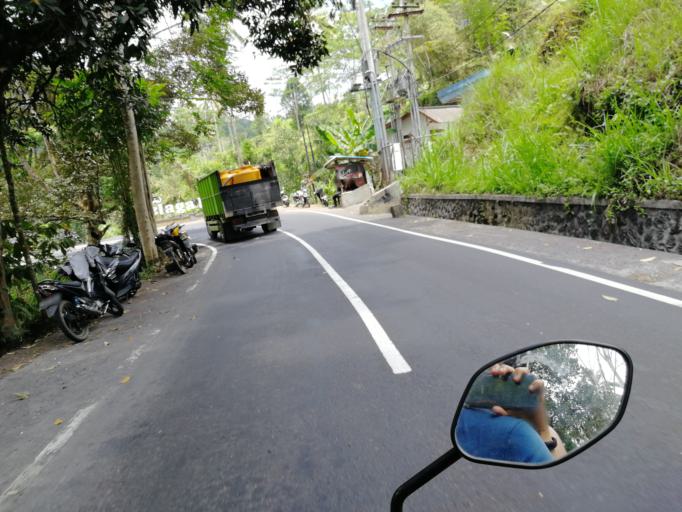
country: ID
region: Bali
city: Banjar Geriana Kangin
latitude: -8.4233
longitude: 115.4341
